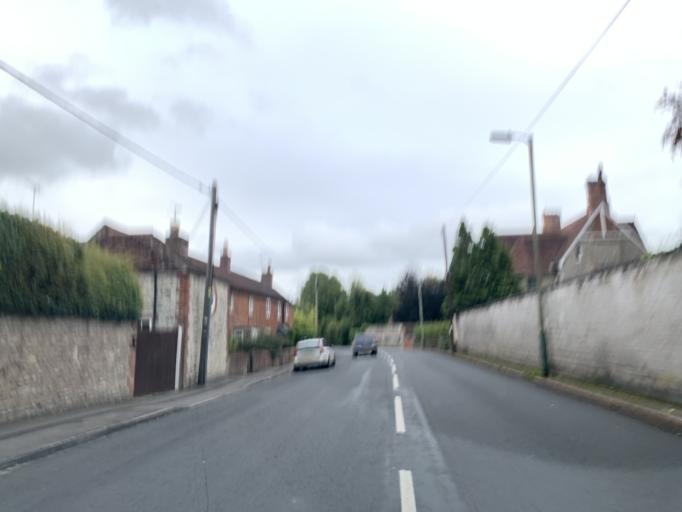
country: GB
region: England
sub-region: Wiltshire
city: Bishopstrow
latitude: 51.1969
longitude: -2.1543
